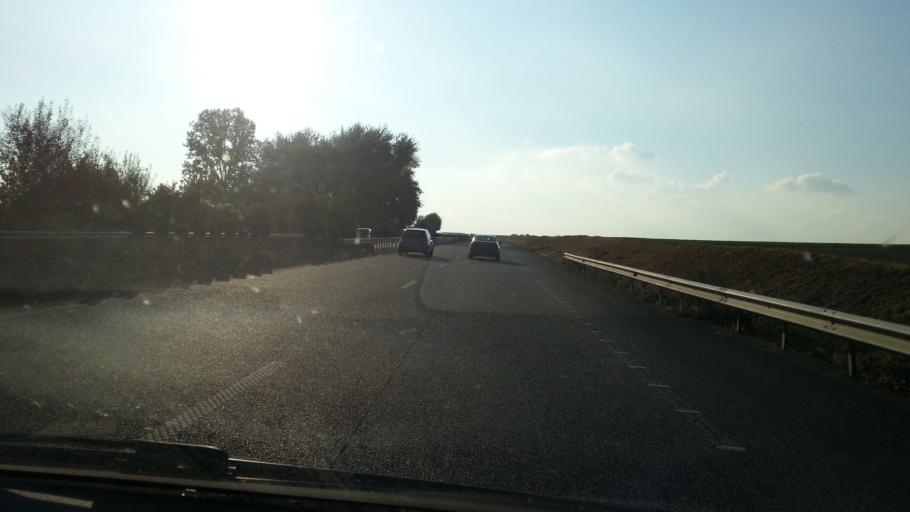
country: FR
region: Picardie
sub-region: Departement de l'Oise
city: Longueil-Annel
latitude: 49.4755
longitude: 2.8443
